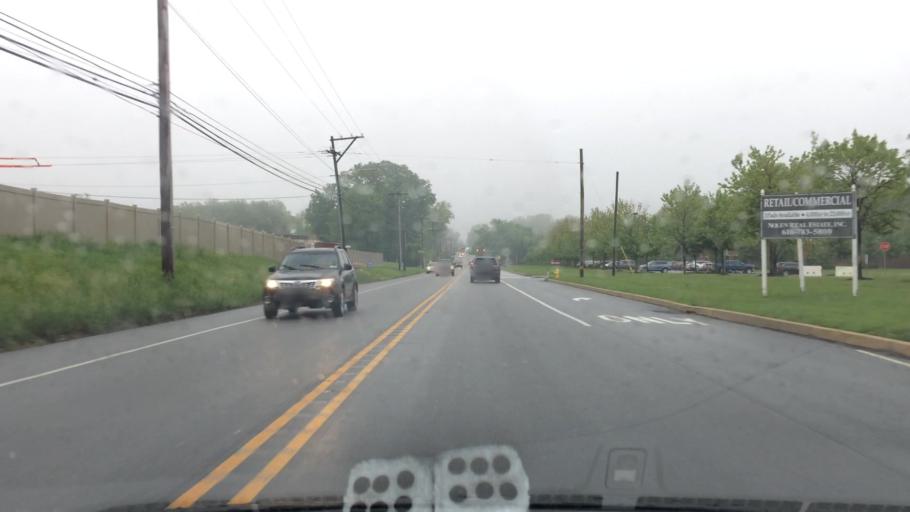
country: US
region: Pennsylvania
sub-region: Delaware County
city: Village Green-Green Ridge
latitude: 39.8557
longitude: -75.4268
